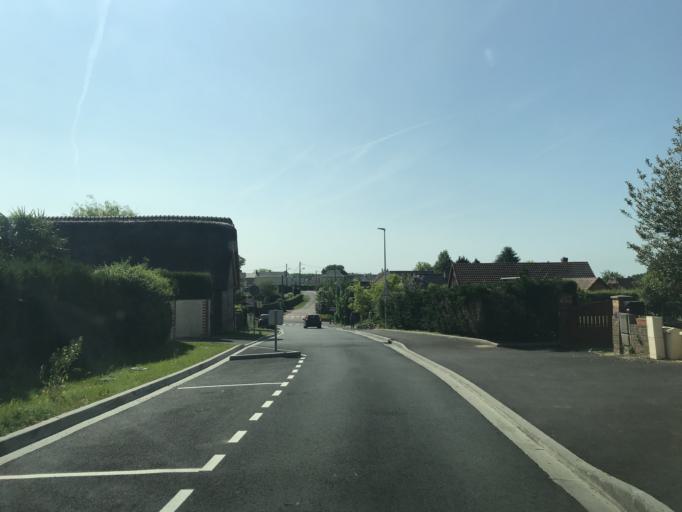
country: FR
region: Haute-Normandie
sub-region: Departement de la Seine-Maritime
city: Ymare
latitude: 49.3648
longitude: 1.1595
